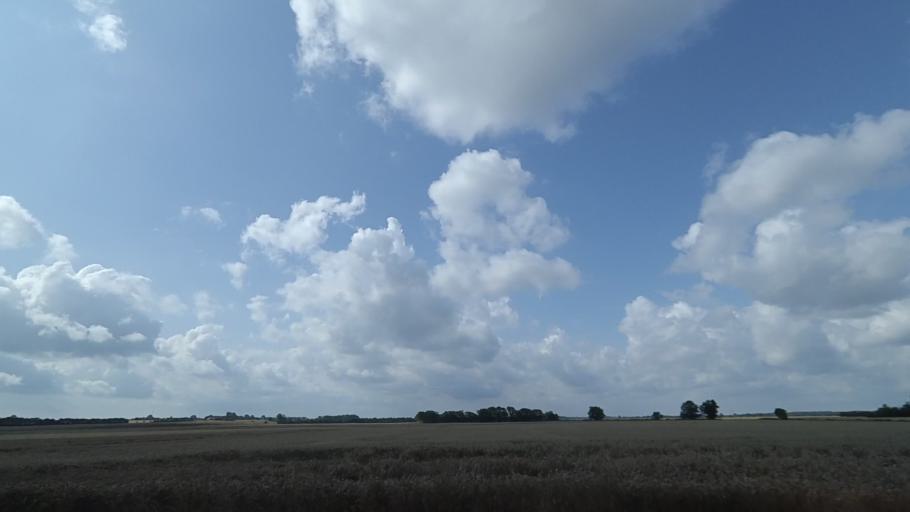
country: DK
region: Central Jutland
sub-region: Norddjurs Kommune
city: Auning
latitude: 56.5030
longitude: 10.4264
